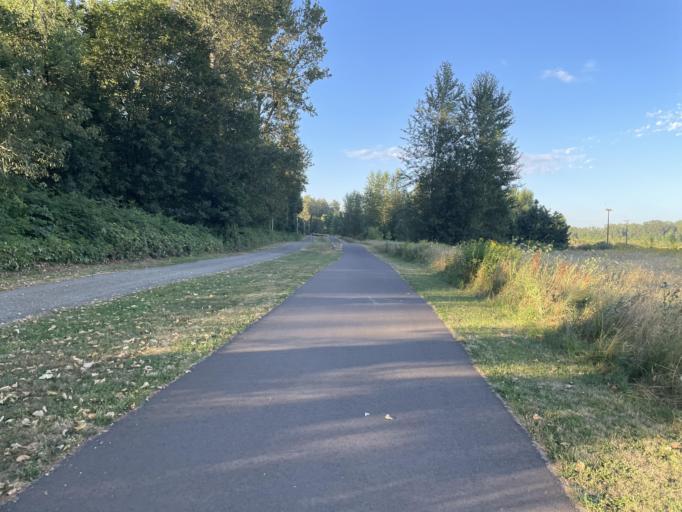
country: US
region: Oregon
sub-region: Marion County
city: Salem
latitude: 44.9257
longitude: -123.0710
